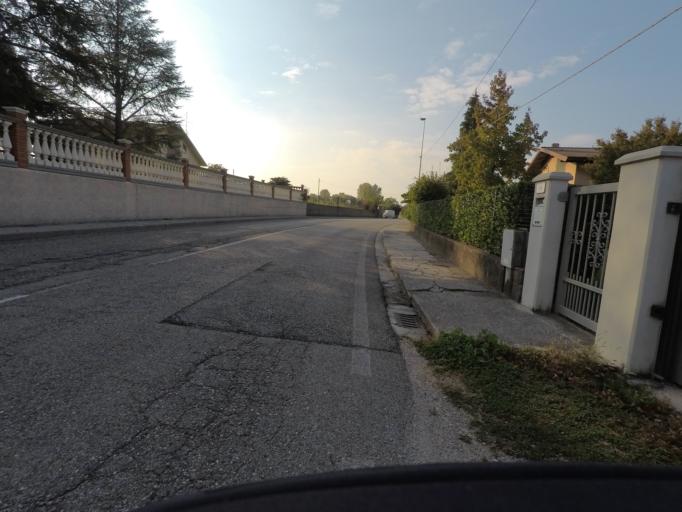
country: IT
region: Friuli Venezia Giulia
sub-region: Provincia di Udine
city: Gemona
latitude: 46.2659
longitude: 13.1424
